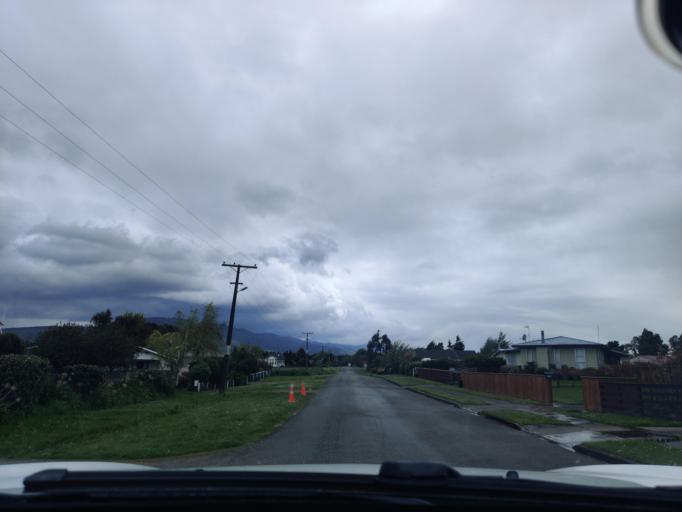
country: NZ
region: Manawatu-Wanganui
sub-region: Palmerston North City
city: Palmerston North
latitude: -40.3341
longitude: 175.8650
